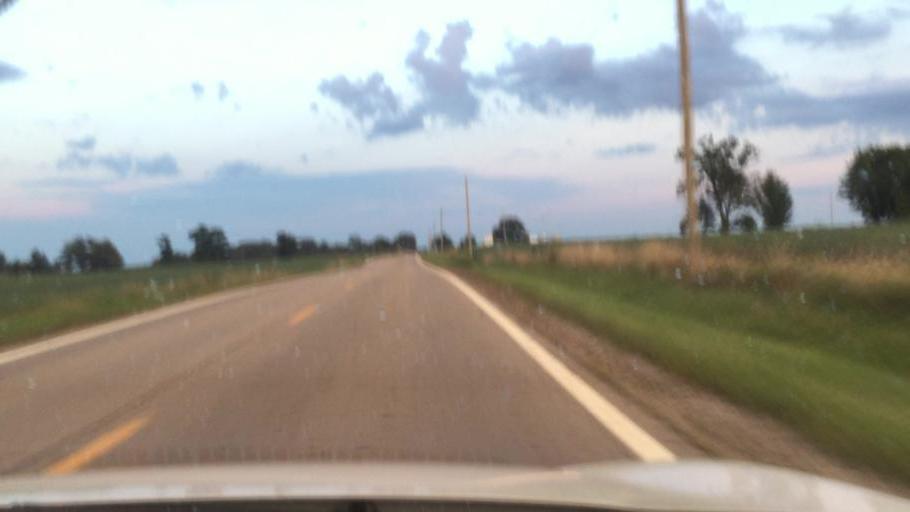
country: US
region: Ohio
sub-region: Madison County
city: Choctaw Lake
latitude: 40.0307
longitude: -83.4892
